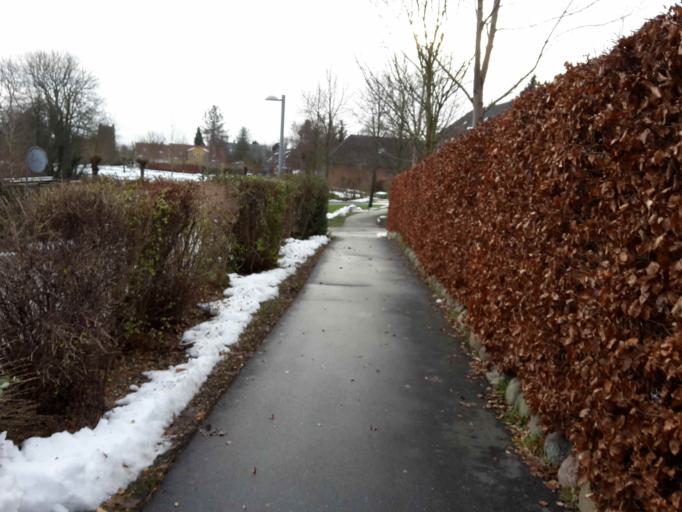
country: DK
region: Capital Region
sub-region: Allerod Kommune
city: Blovstrod
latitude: 55.8676
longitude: 12.3874
